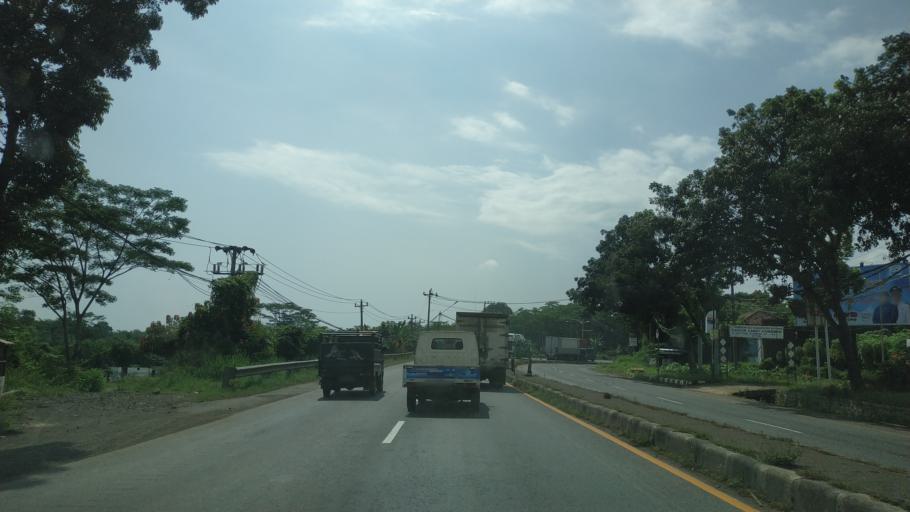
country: ID
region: Central Java
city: Pekalongan
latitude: -6.9246
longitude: 109.7606
